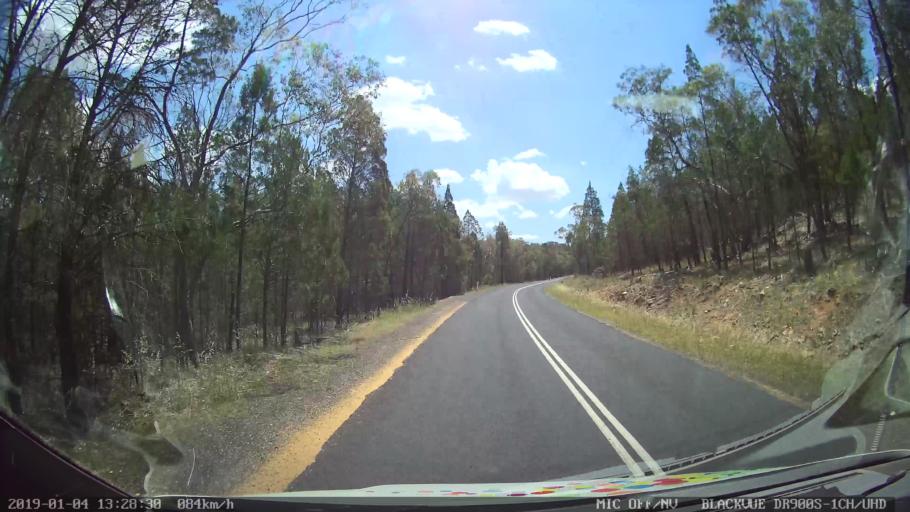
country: AU
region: New South Wales
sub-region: Parkes
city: Peak Hill
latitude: -32.6581
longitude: 148.5505
